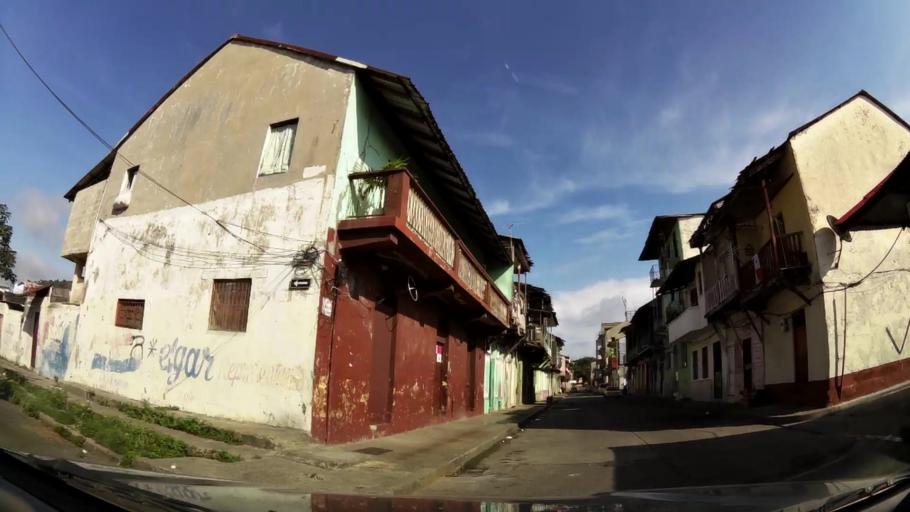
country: PA
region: Panama
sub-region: Distrito de Panama
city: Ancon
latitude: 8.9507
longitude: -79.5389
